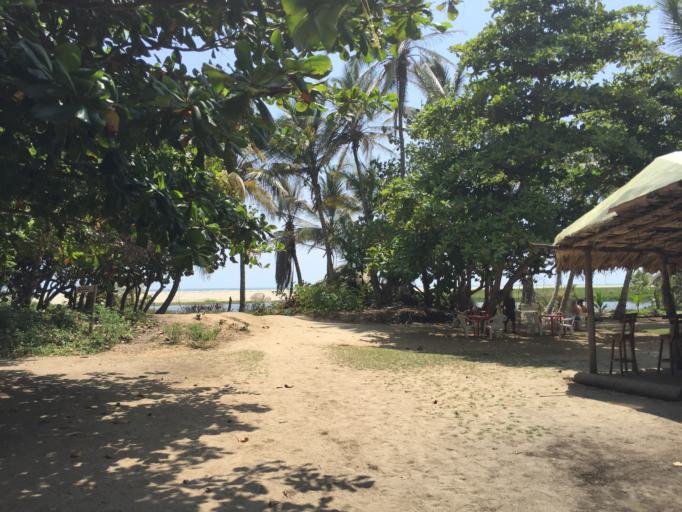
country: CO
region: Magdalena
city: Santa Marta
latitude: 11.3172
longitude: -73.9530
